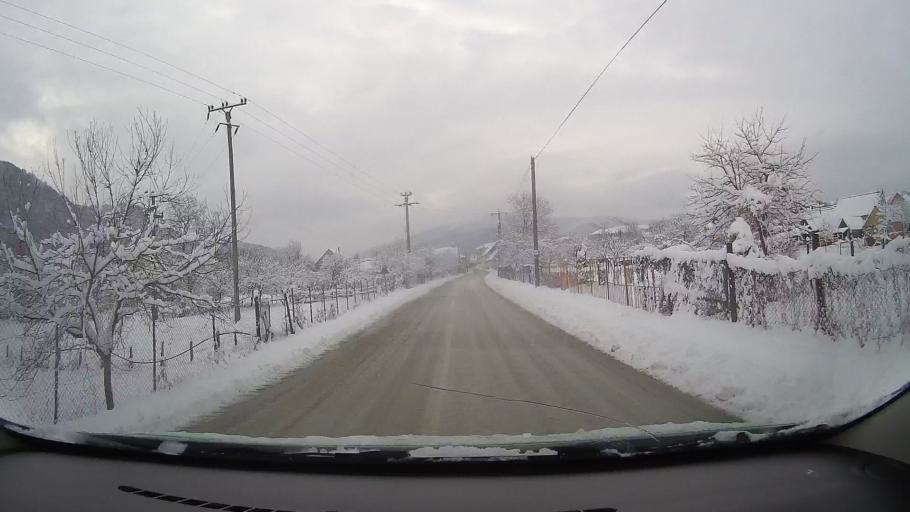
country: RO
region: Alba
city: Pianu de Sus
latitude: 45.9051
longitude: 23.4803
